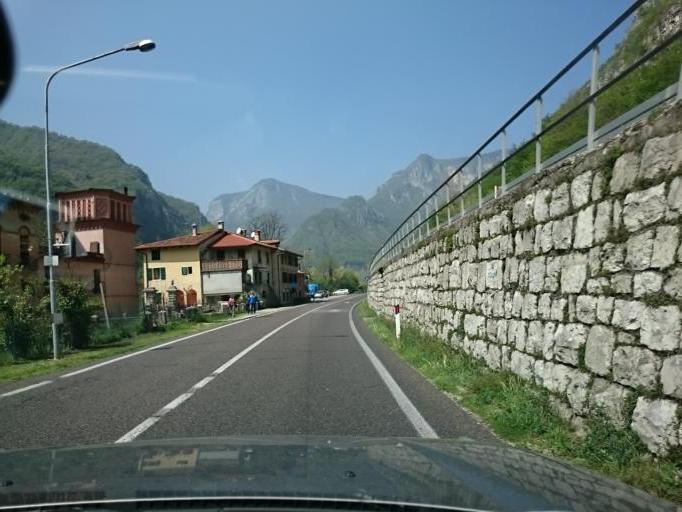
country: IT
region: Veneto
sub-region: Provincia di Vicenza
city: Valstagna
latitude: 45.8486
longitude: 11.6704
